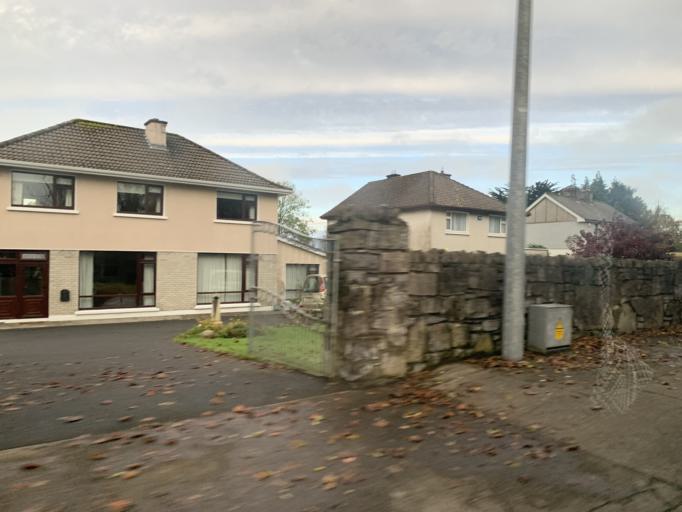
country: IE
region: Connaught
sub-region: Sligo
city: Sligo
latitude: 54.2718
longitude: -8.5074
